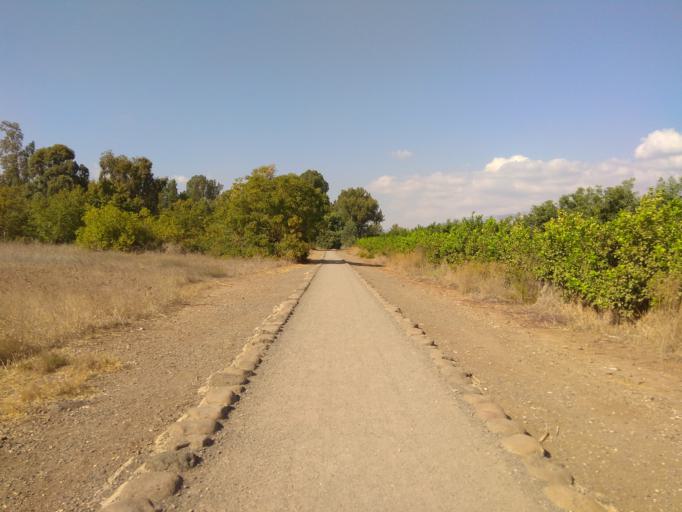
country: IL
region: Northern District
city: Qiryat Shemona
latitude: 33.2246
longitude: 35.6159
